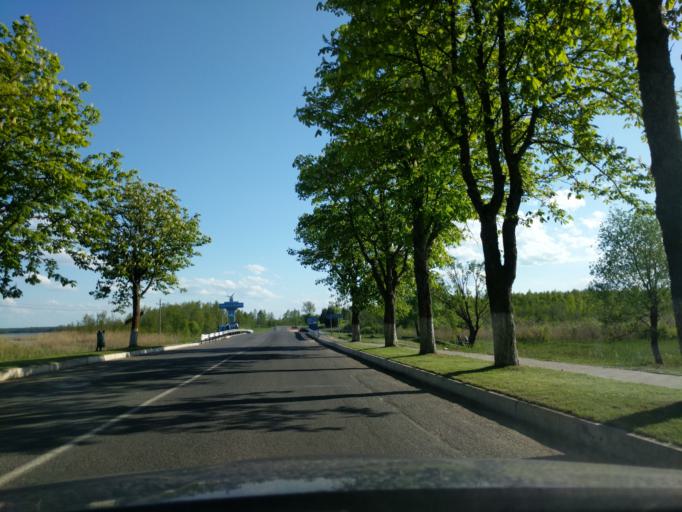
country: BY
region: Minsk
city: Myadzyel
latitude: 54.8648
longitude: 26.9333
